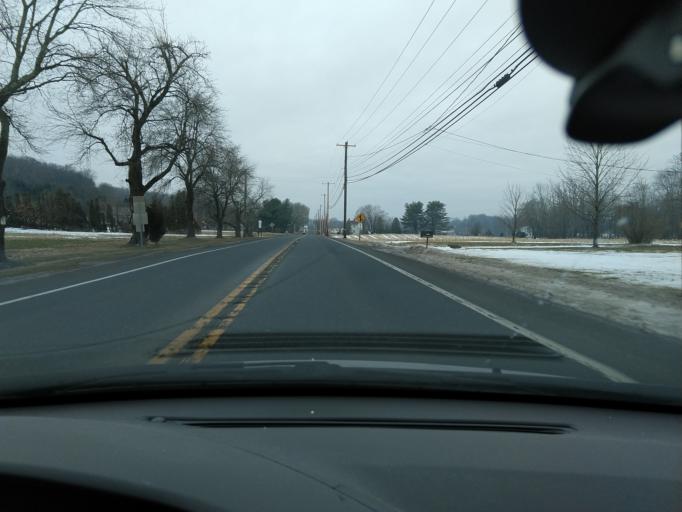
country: US
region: Pennsylvania
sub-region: Lehigh County
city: Macungie
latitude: 40.4824
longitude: -75.5245
